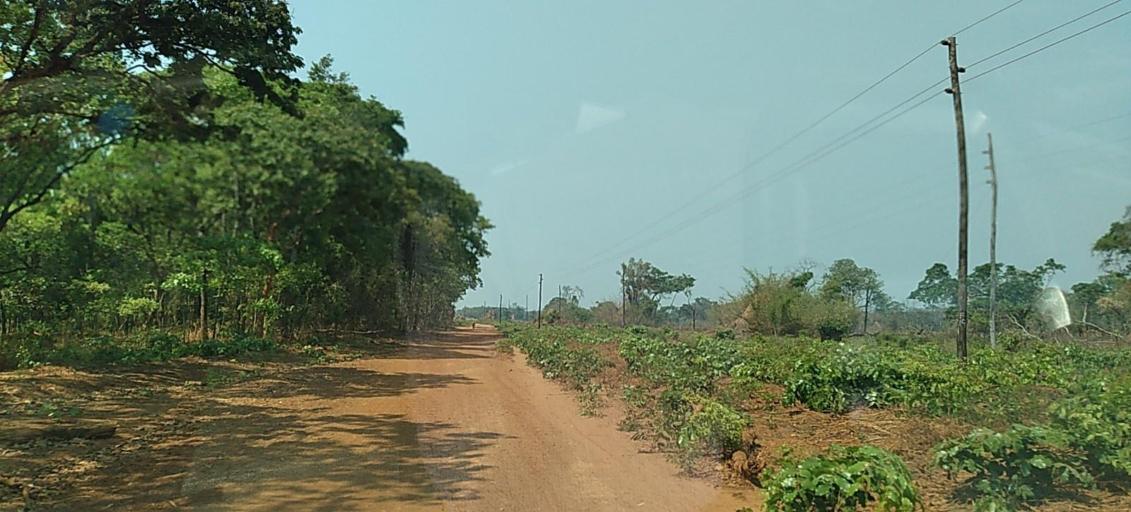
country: ZM
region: Copperbelt
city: Kalulushi
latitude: -13.0858
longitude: 27.4093
